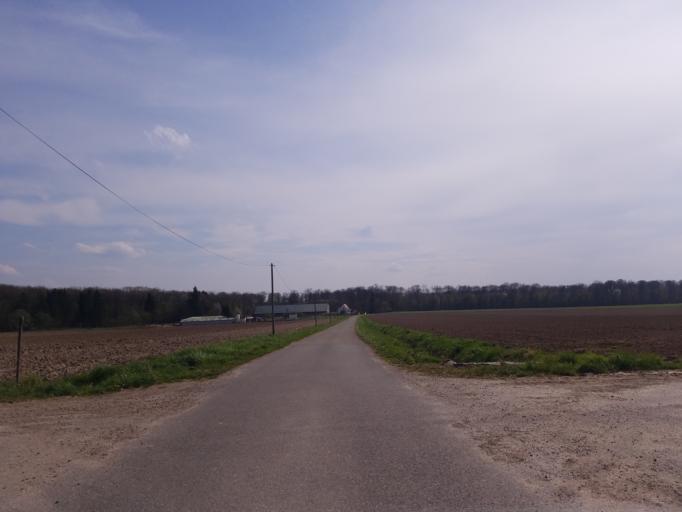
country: FR
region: Alsace
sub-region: Departement du Bas-Rhin
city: Betschdorf
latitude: 48.8949
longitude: 7.9544
